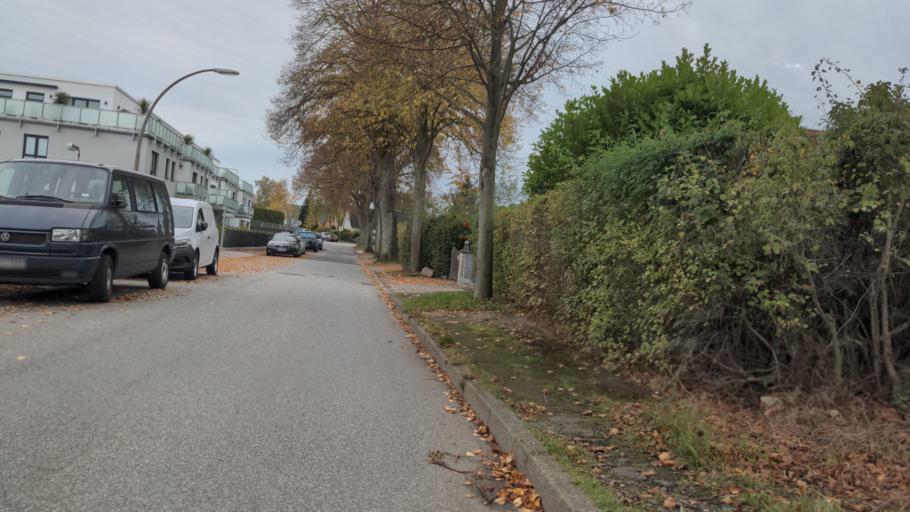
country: DE
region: Schleswig-Holstein
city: Stockelsdorf
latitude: 53.9107
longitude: 10.6674
